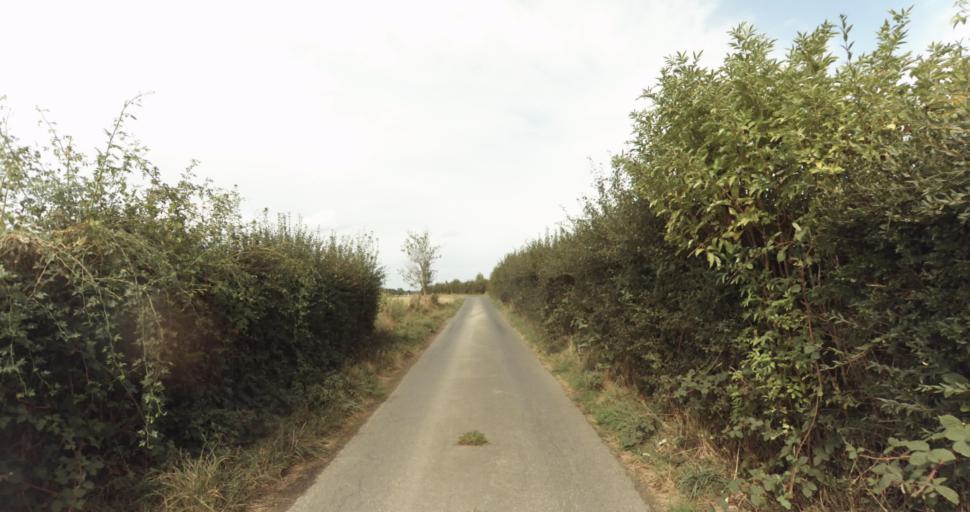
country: FR
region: Lower Normandy
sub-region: Departement du Calvados
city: Orbec
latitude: 48.9486
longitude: 0.3995
